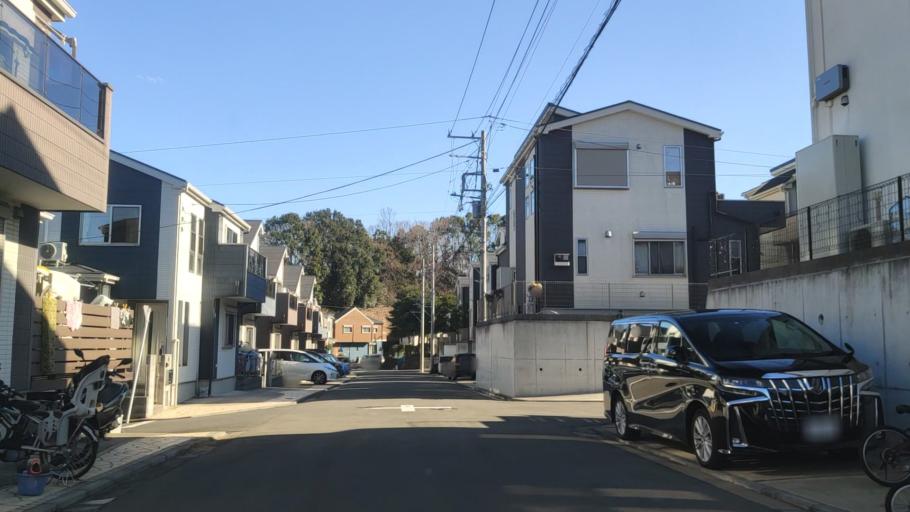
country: JP
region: Kanagawa
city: Minami-rinkan
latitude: 35.5060
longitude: 139.5264
